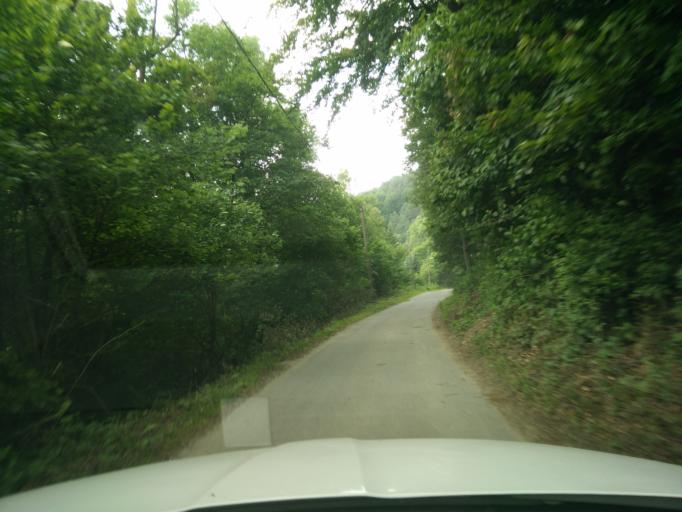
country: SK
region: Nitriansky
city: Bojnice
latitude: 48.8920
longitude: 18.5468
